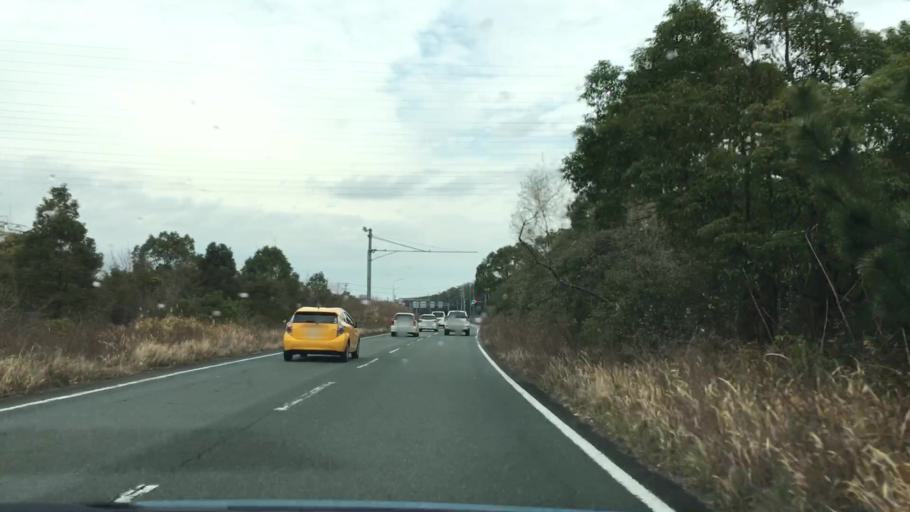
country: JP
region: Aichi
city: Toyohashi
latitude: 34.7119
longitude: 137.3363
